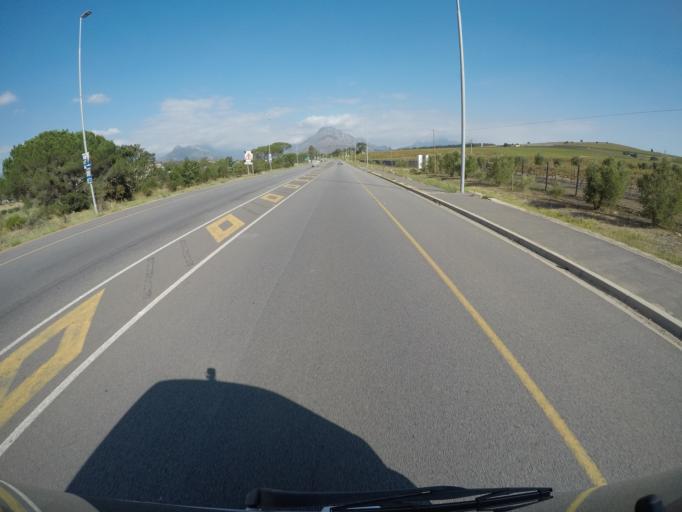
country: ZA
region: Western Cape
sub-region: Cape Winelands District Municipality
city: Stellenbosch
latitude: -33.9001
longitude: 18.8384
